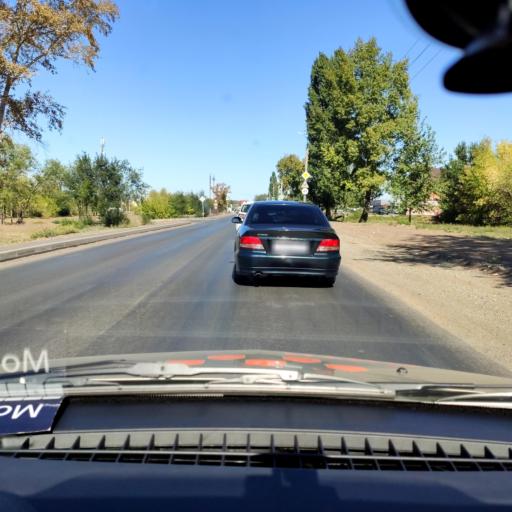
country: RU
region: Orenburg
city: Tatarskaya Kargala
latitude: 51.8653
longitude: 55.1395
